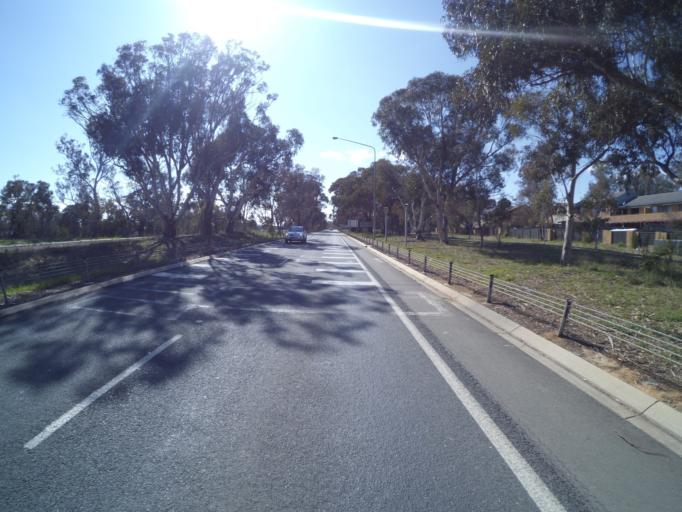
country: AU
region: Australian Capital Territory
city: Kaleen
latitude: -35.2243
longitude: 149.1670
